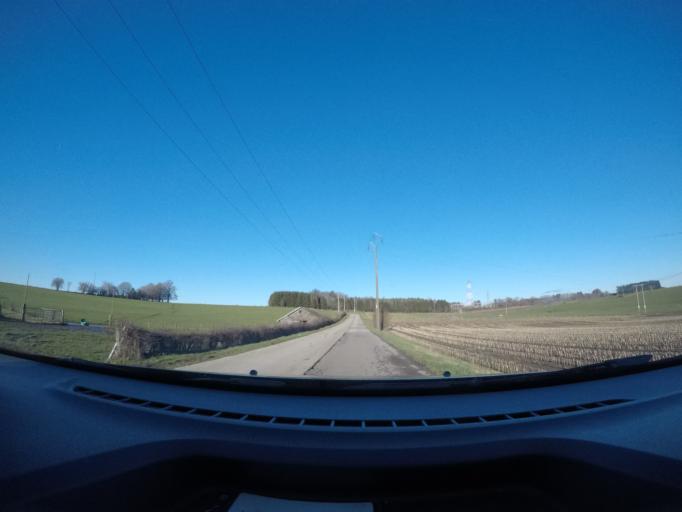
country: BE
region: Wallonia
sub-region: Province du Luxembourg
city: Bertrix
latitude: 49.8426
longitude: 5.2992
